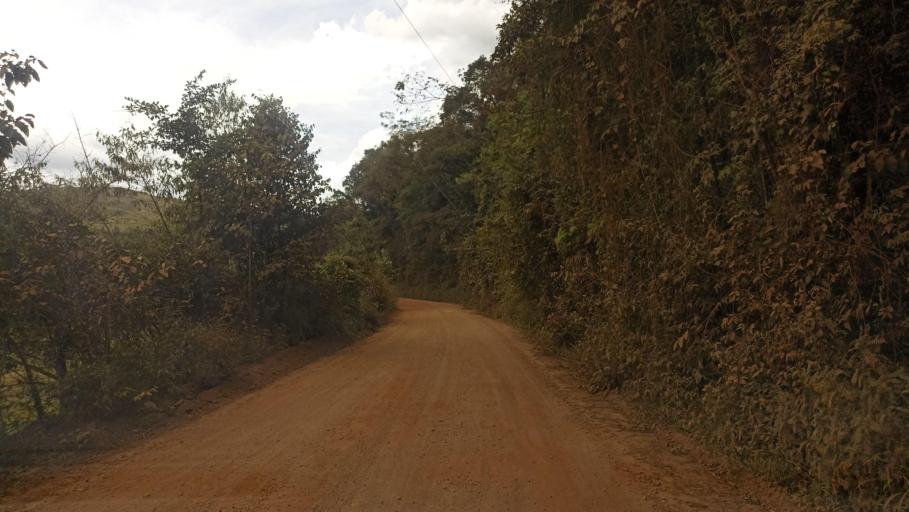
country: BR
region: Minas Gerais
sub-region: Itabirito
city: Itabirito
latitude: -20.3573
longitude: -43.7696
